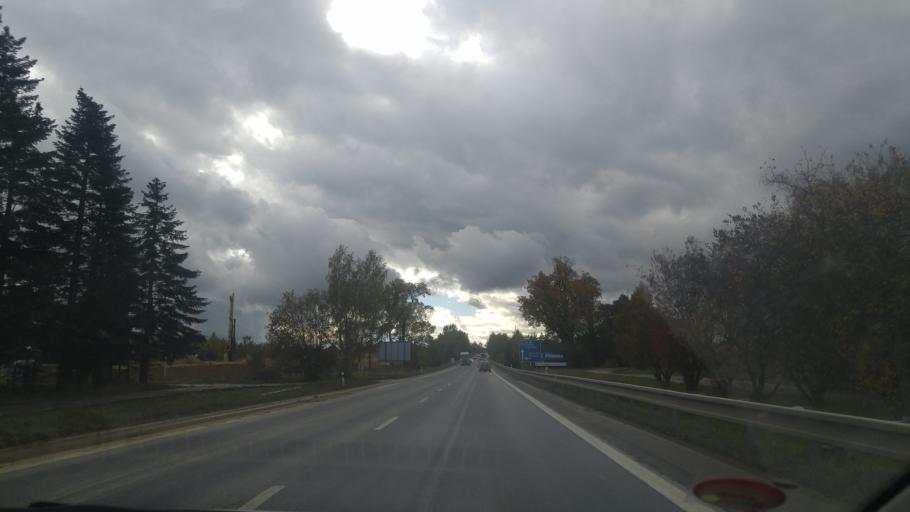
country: CZ
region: Jihocesky
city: Sevetin
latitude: 49.1309
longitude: 14.6088
